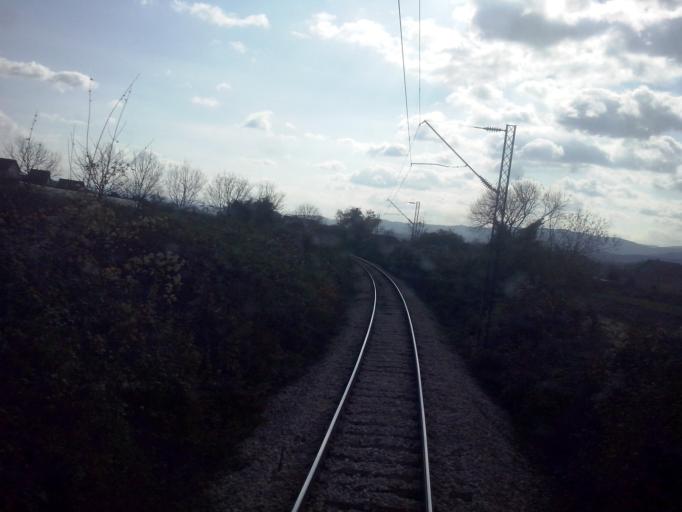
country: RS
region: Central Serbia
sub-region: Zlatiborski Okrug
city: Pozega
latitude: 43.8748
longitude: 20.0004
